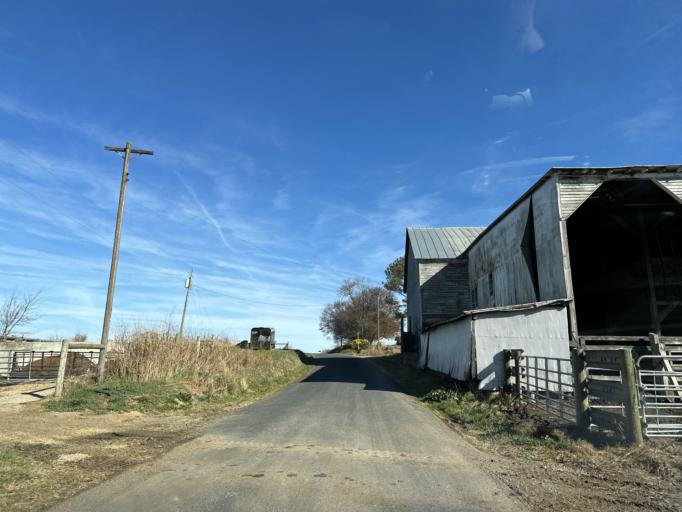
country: US
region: Virginia
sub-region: Augusta County
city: Weyers Cave
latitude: 38.2647
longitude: -78.9272
